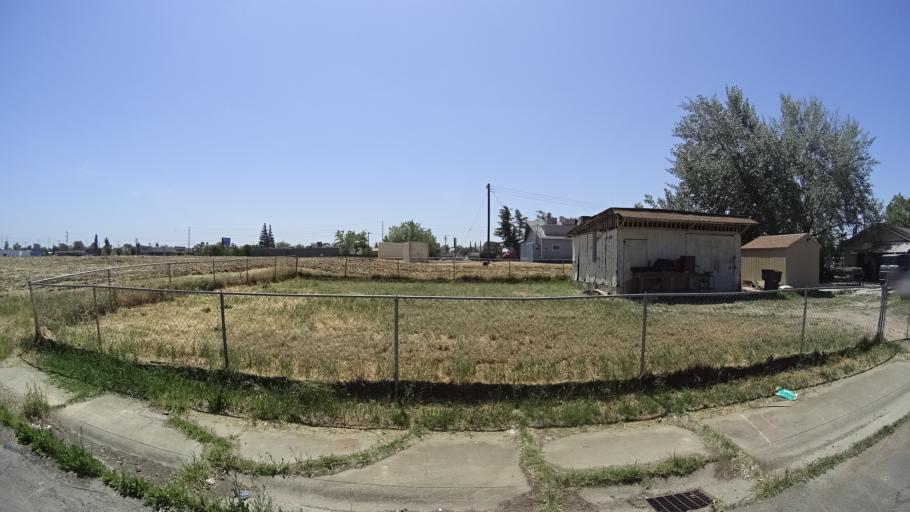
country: US
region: California
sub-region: Sacramento County
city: Parkway
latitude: 38.4976
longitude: -121.4784
